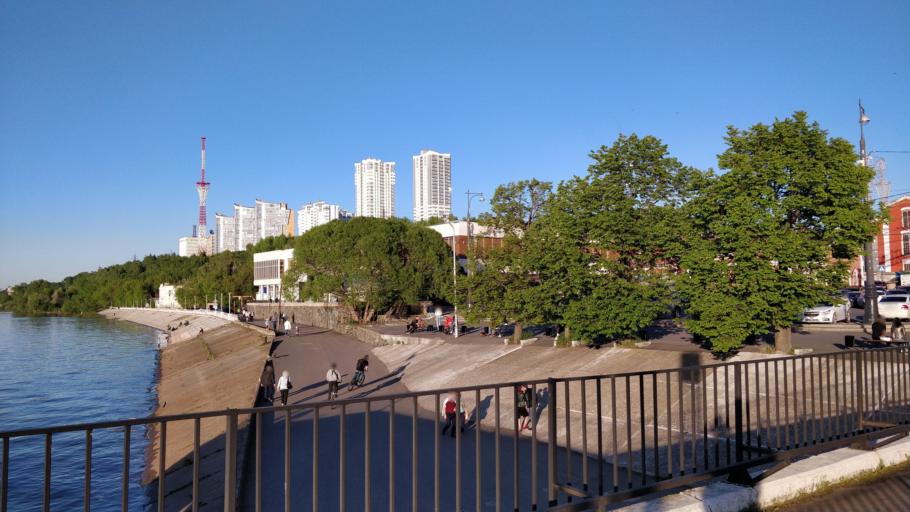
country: RU
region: Perm
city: Perm
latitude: 58.0216
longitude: 56.2525
